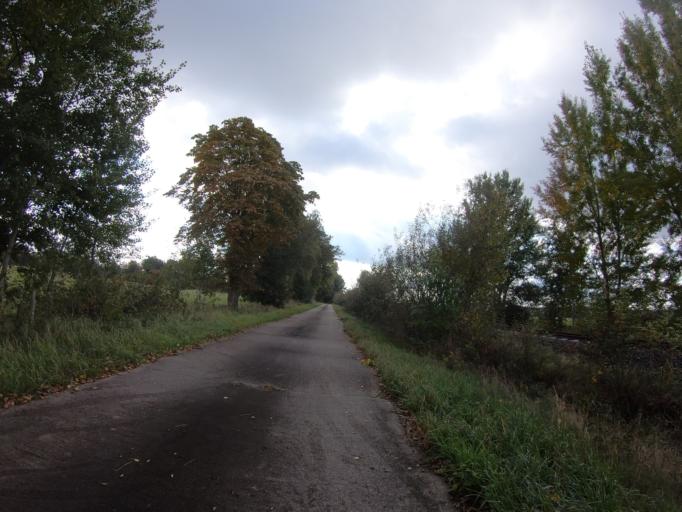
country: DE
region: Lower Saxony
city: Wahrenholz
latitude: 52.5804
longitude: 10.6104
